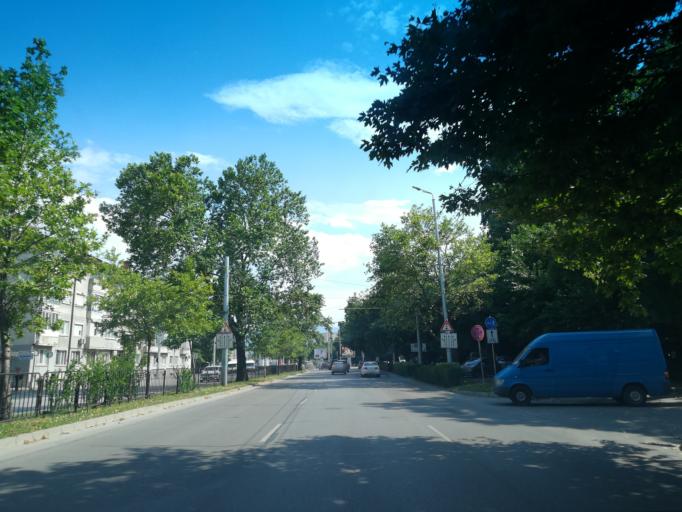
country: BG
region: Plovdiv
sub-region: Obshtina Plovdiv
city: Plovdiv
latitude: 42.1376
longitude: 24.7629
